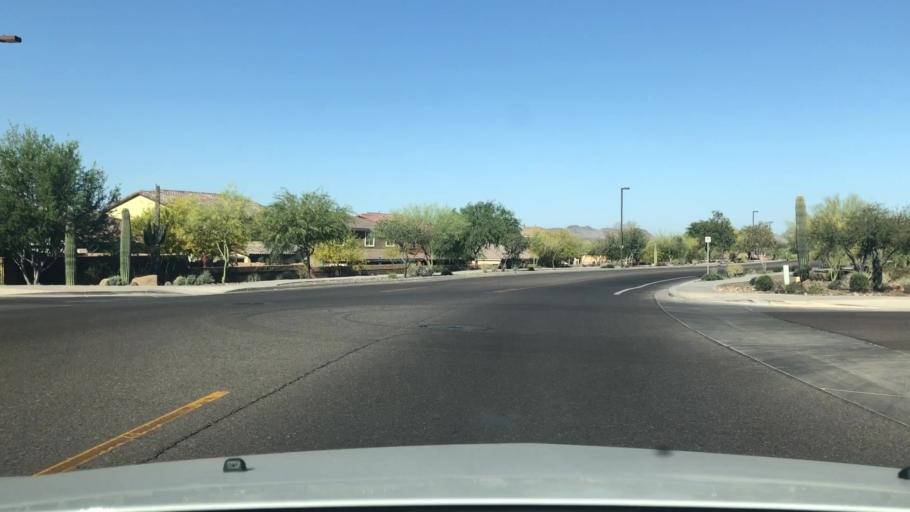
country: US
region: Arizona
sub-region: Maricopa County
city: Anthem
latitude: 33.7307
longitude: -112.0966
